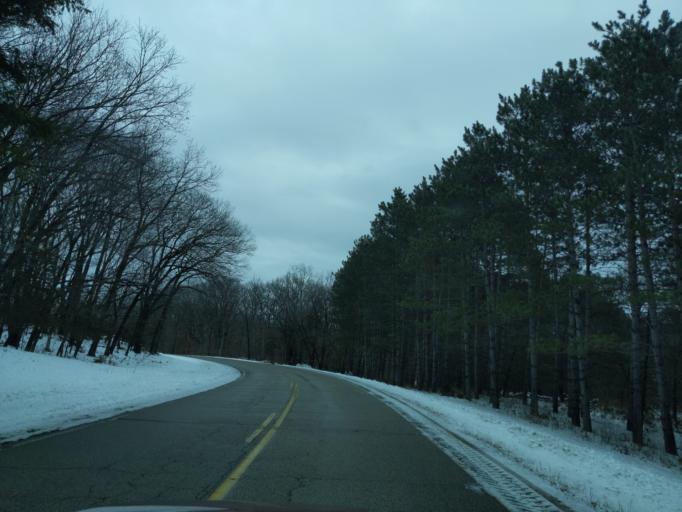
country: US
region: Wisconsin
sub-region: Marquette County
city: Montello
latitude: 43.9151
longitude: -89.3352
